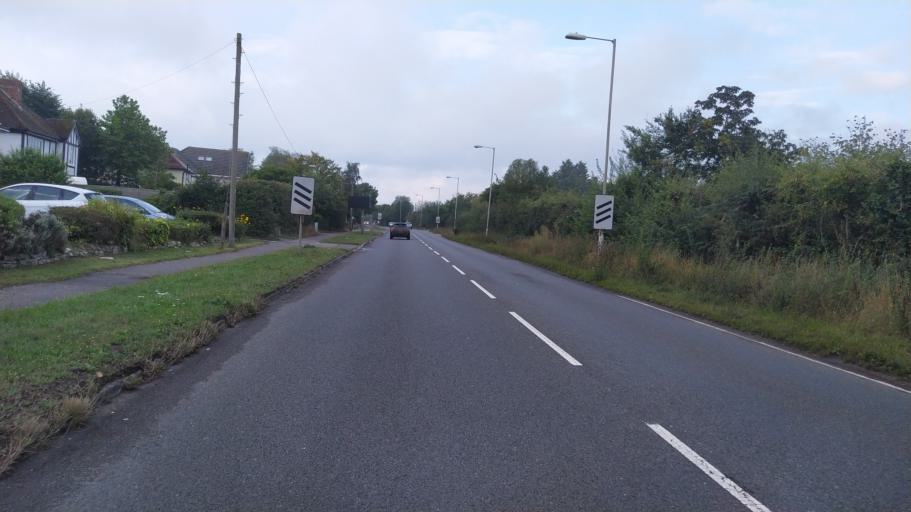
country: GB
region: England
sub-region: Hampshire
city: Bransgore
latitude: 50.7463
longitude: -1.7359
